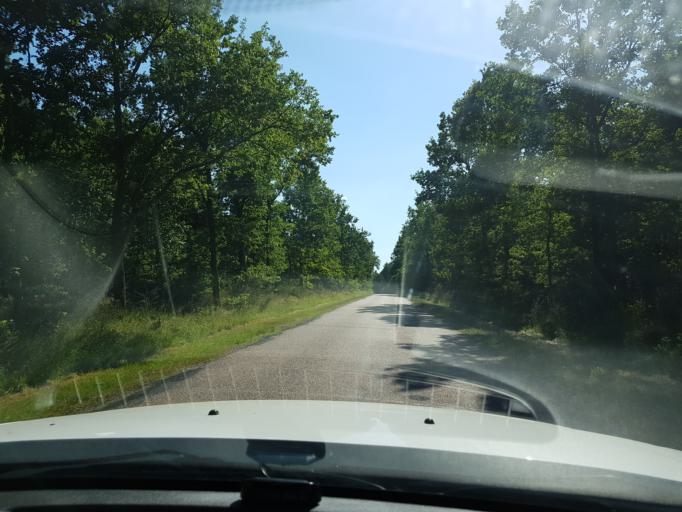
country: PL
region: West Pomeranian Voivodeship
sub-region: Powiat swidwinski
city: Slawoborze
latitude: 53.9231
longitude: 15.7971
